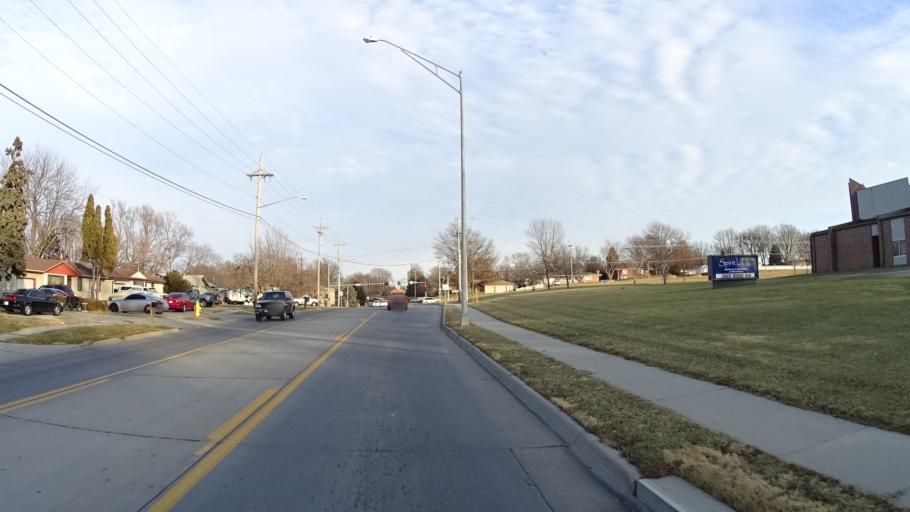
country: US
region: Nebraska
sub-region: Sarpy County
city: La Vista
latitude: 41.1908
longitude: -95.9887
